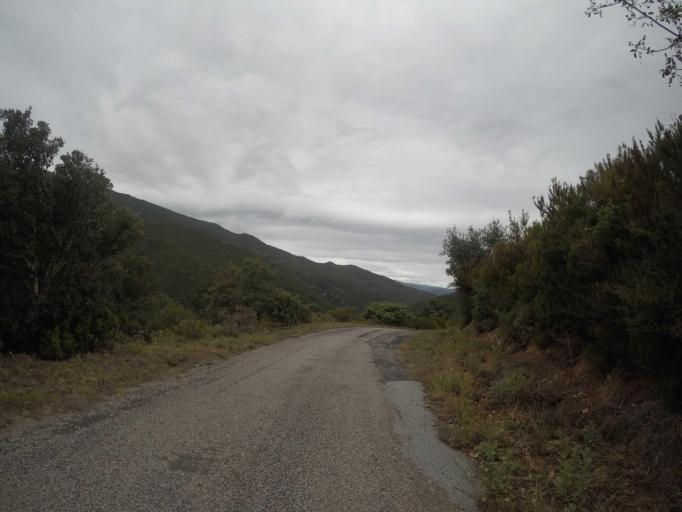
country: FR
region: Languedoc-Roussillon
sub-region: Departement des Pyrenees-Orientales
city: Ille-sur-Tet
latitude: 42.6144
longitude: 2.6061
